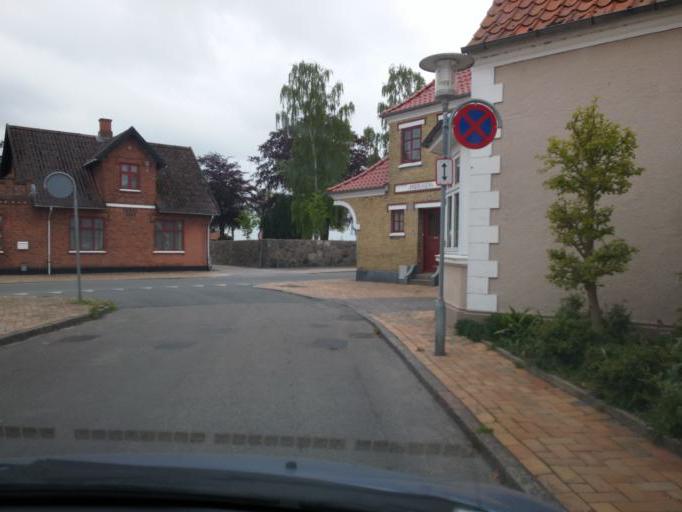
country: DK
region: South Denmark
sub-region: Kerteminde Kommune
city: Kerteminde
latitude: 55.4492
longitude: 10.6529
